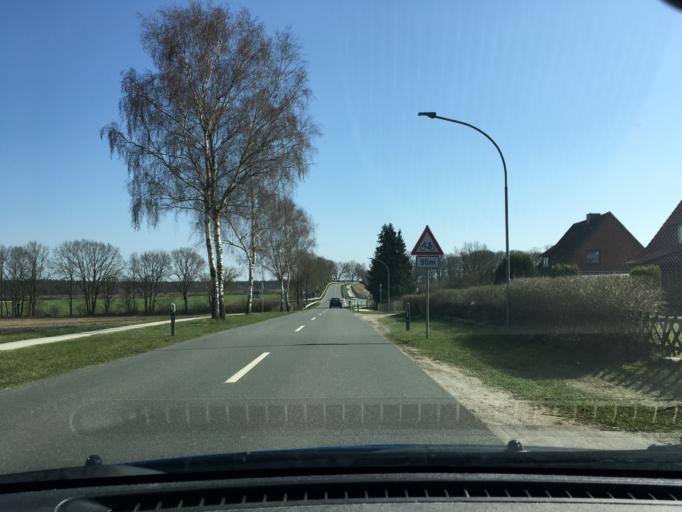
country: DE
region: Lower Saxony
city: Wriedel
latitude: 53.0080
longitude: 10.2890
